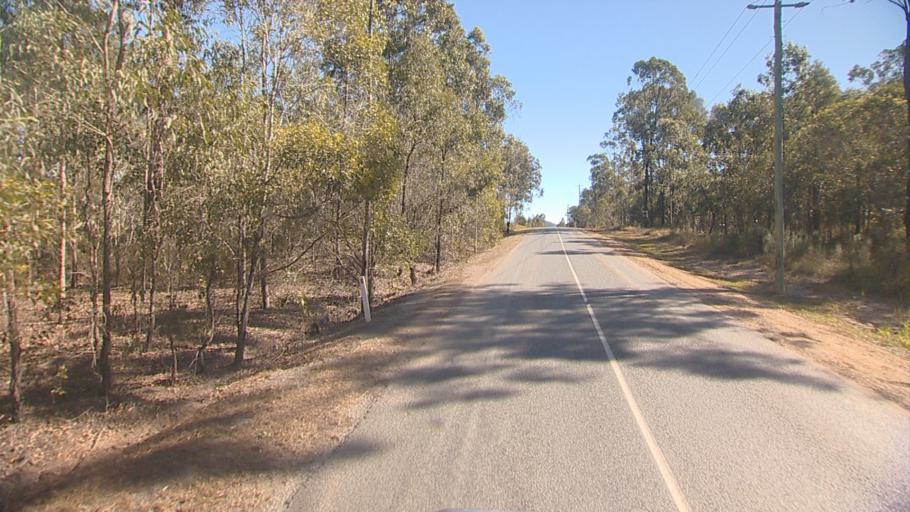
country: AU
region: Queensland
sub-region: Ipswich
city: Springfield Lakes
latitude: -27.7317
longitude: 152.9394
